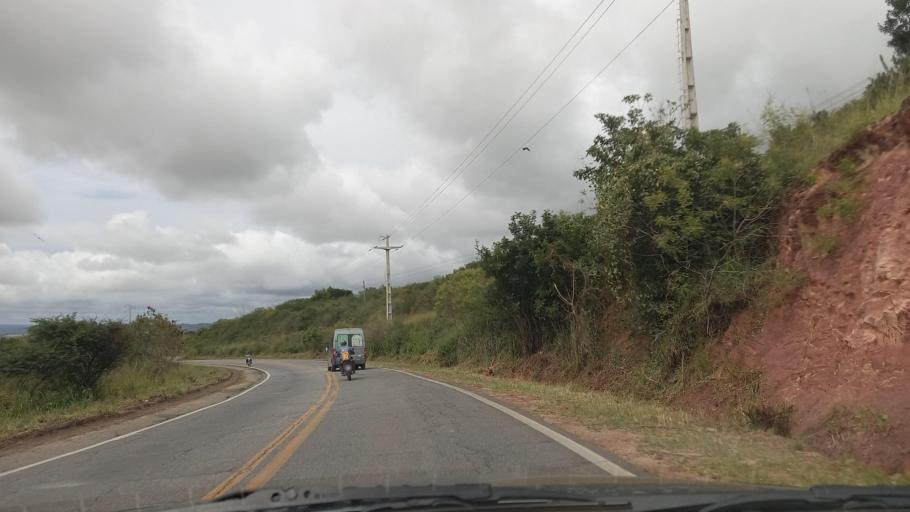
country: BR
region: Pernambuco
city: Garanhuns
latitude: -8.8777
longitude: -36.4517
